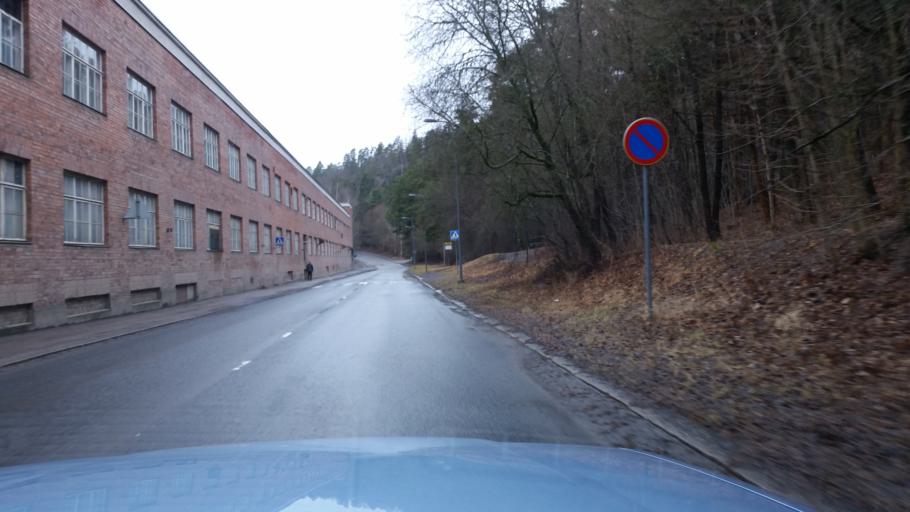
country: FI
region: Pirkanmaa
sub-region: Tampere
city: Tampere
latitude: 61.4934
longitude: 23.7258
